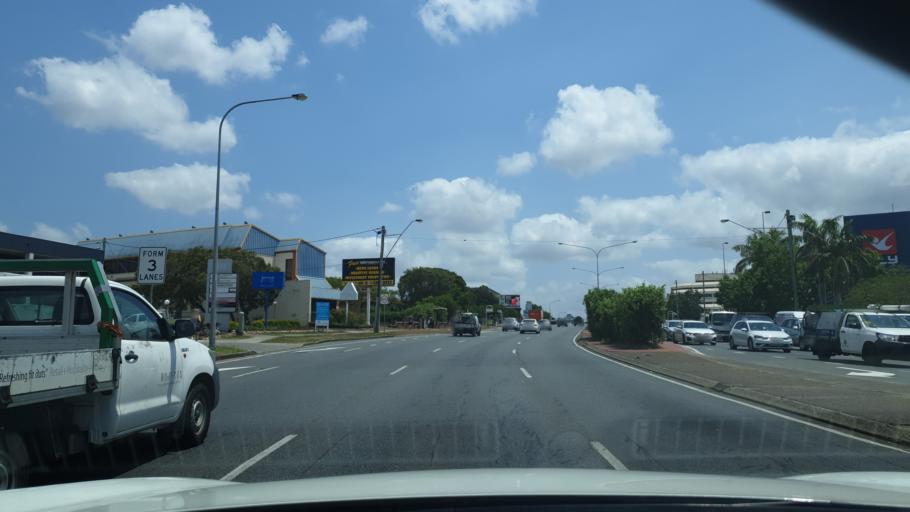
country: AU
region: Queensland
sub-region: Brisbane
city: Chermside West
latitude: -27.3845
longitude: 153.0303
